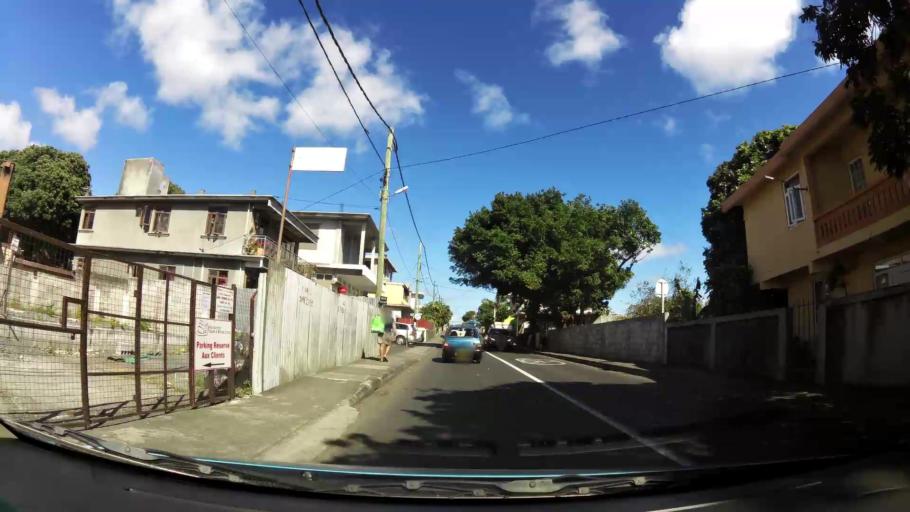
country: MU
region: Plaines Wilhems
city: Vacoas
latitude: -20.3120
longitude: 57.4890
